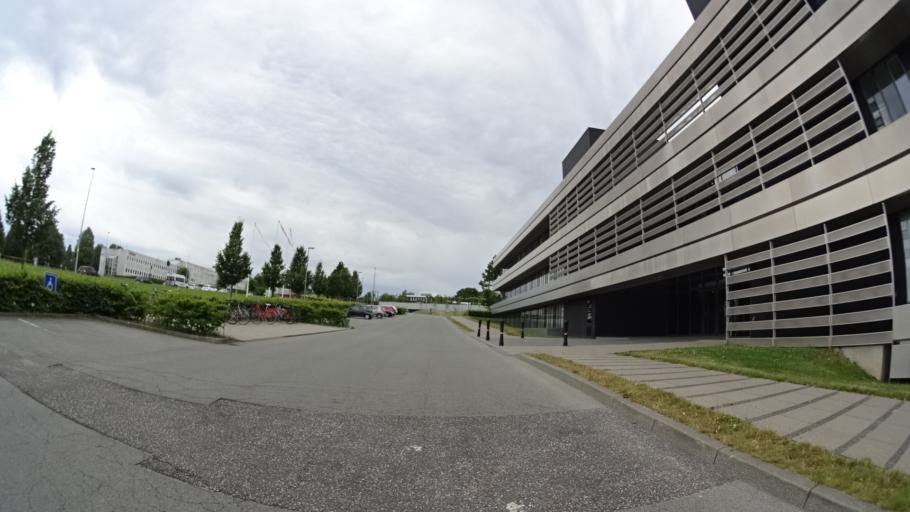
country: DK
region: Central Jutland
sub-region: Arhus Kommune
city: Stavtrup
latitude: 56.1240
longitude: 10.1524
